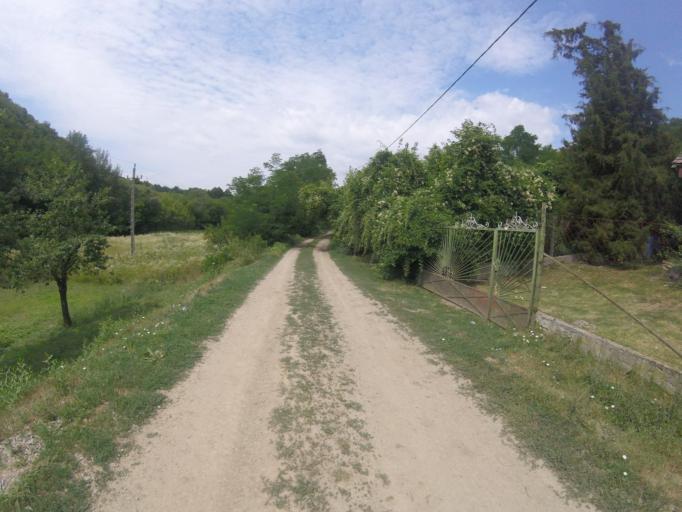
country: HU
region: Nograd
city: Tar
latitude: 47.9517
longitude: 19.7571
